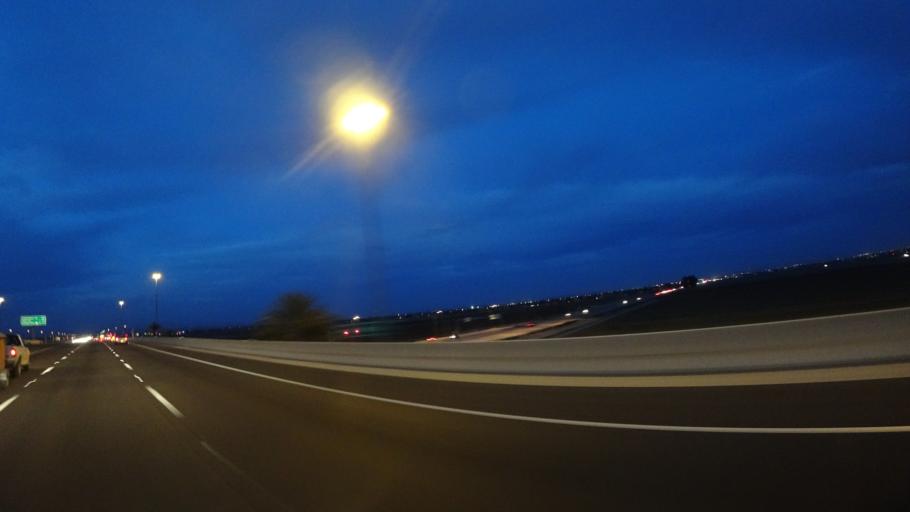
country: US
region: Arizona
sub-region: Maricopa County
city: Citrus Park
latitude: 33.6089
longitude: -112.4179
